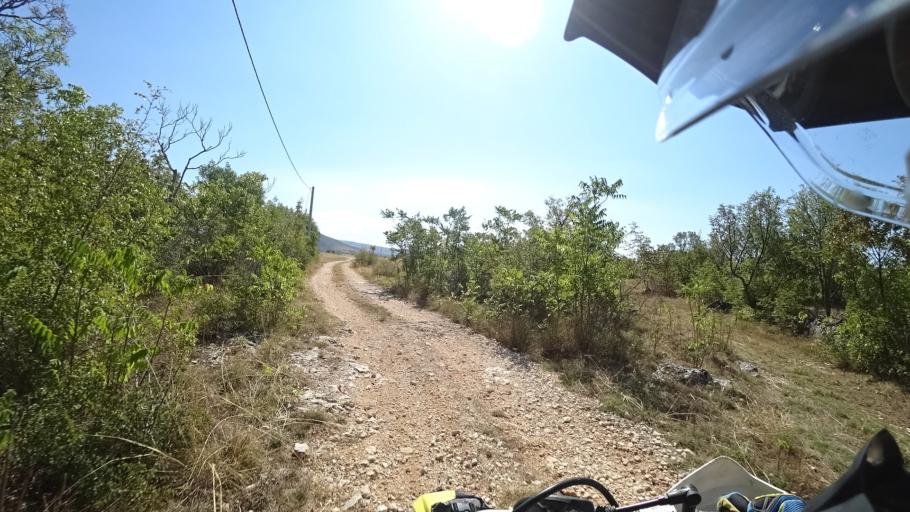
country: HR
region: Sibensko-Kniniska
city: Drnis
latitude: 43.8377
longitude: 16.2917
